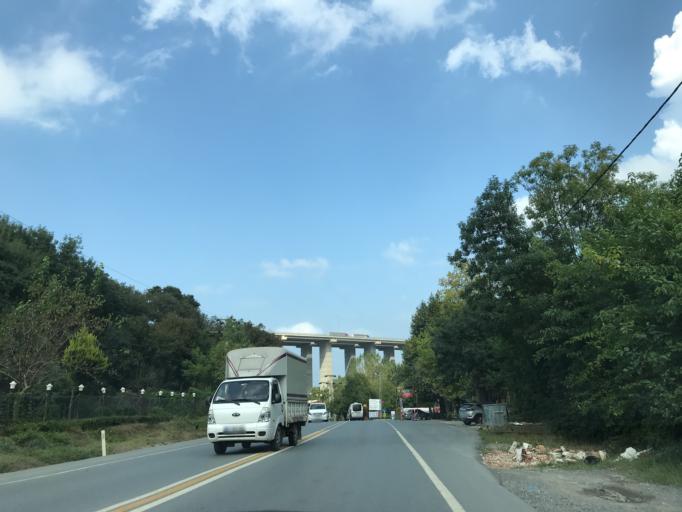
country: TR
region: Istanbul
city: Arikoey
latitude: 41.2227
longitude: 29.0345
